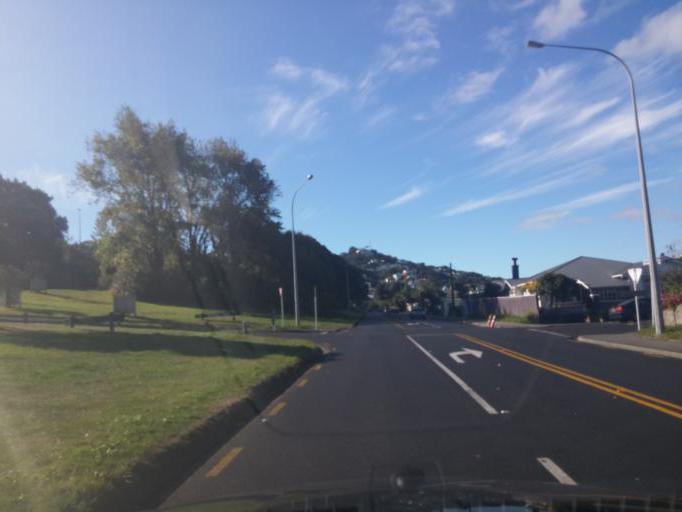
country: NZ
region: Wellington
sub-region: Wellington City
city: Wellington
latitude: -41.3090
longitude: 174.7914
